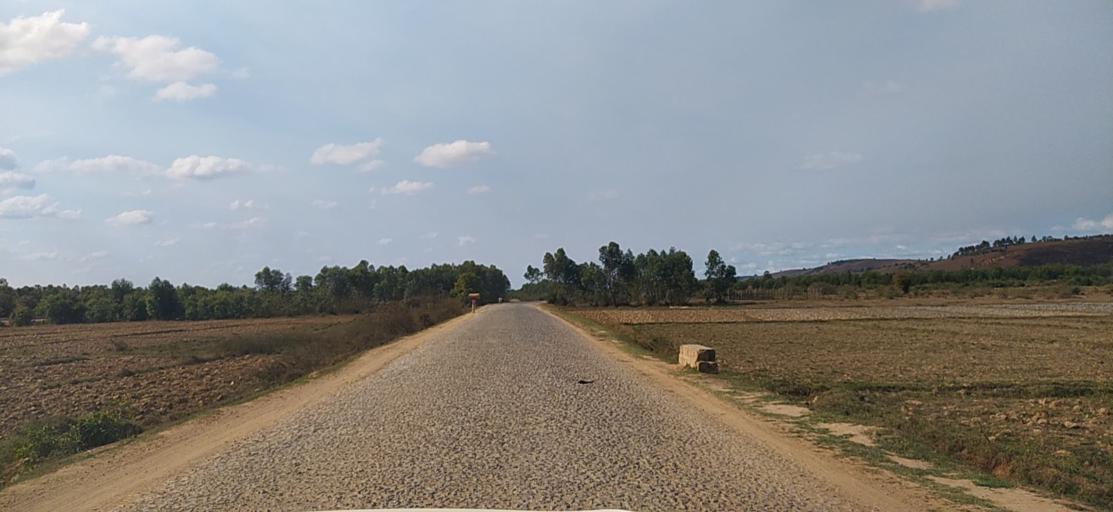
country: MG
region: Alaotra Mangoro
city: Moramanga
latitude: -18.6895
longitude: 48.2711
